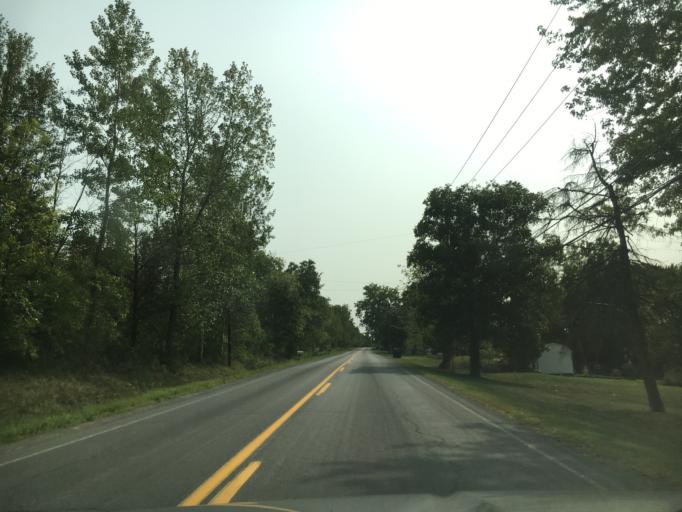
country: US
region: New York
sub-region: Steuben County
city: Sylvan Beach
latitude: 42.4655
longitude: -77.0979
